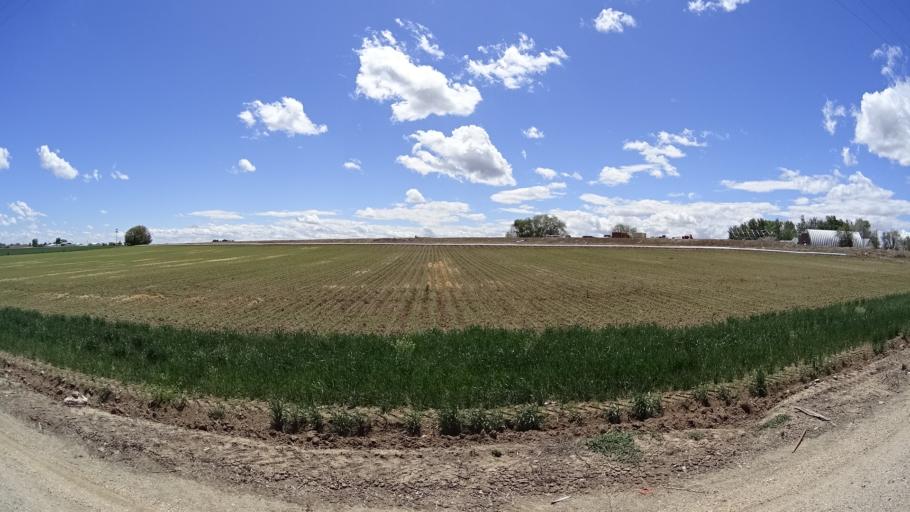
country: US
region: Idaho
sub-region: Ada County
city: Meridian
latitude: 43.5906
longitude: -116.4608
